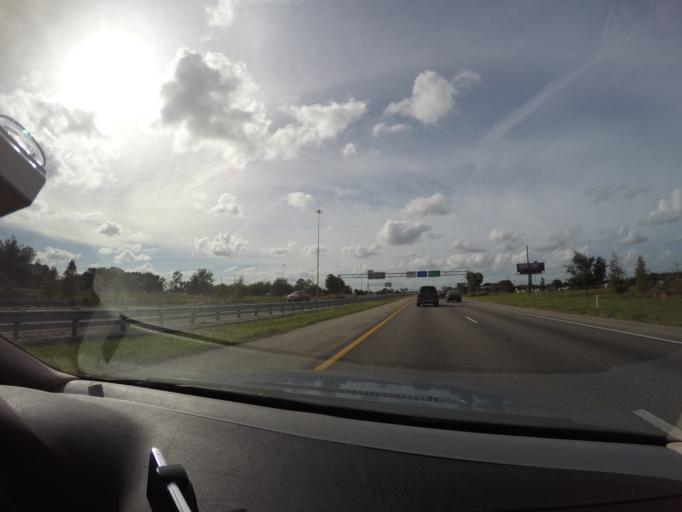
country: US
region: Florida
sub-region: Orange County
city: Belle Isle
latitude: 28.4515
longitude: -81.3119
